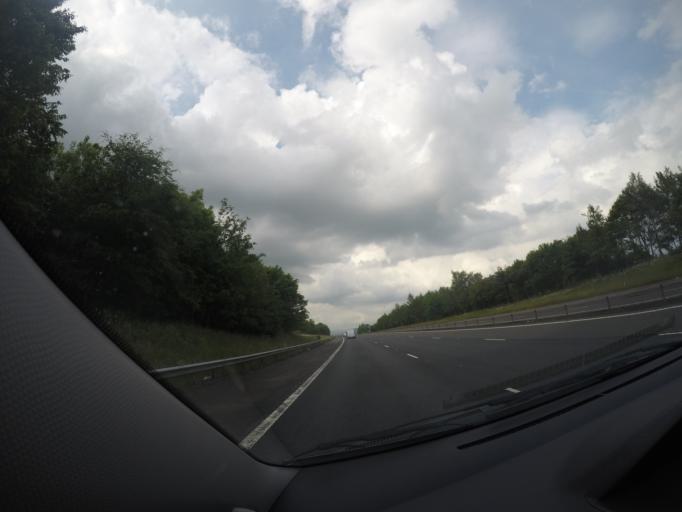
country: GB
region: Scotland
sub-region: Dumfries and Galloway
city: Moffat
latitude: 55.2397
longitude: -3.4099
